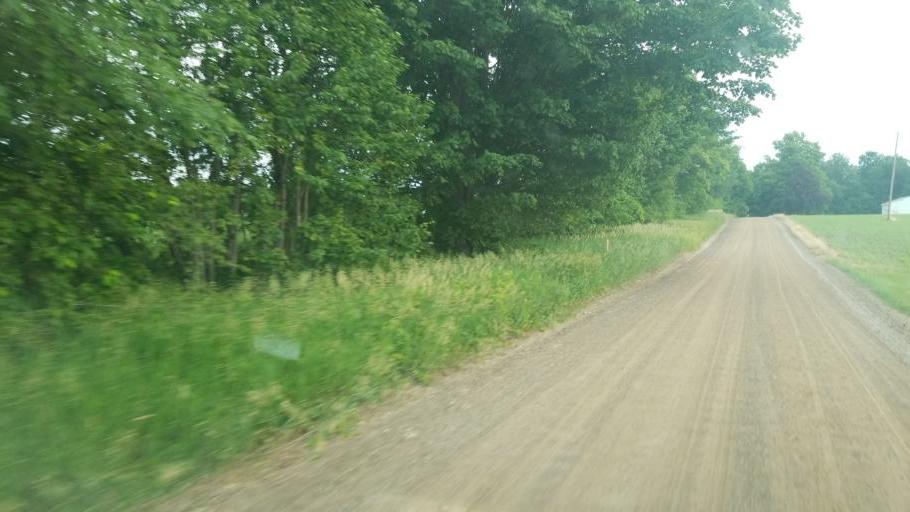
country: US
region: Michigan
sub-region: Barry County
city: Nashville
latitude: 42.6007
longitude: -84.9756
